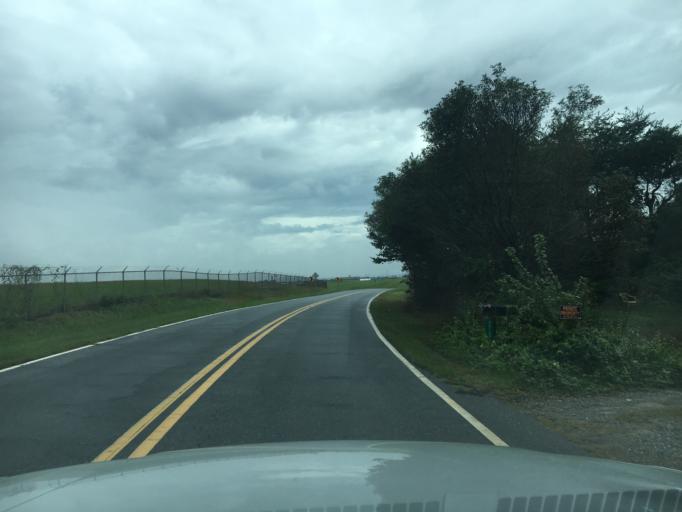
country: US
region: North Carolina
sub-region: Catawba County
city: Longview
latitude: 35.7445
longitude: -81.3834
